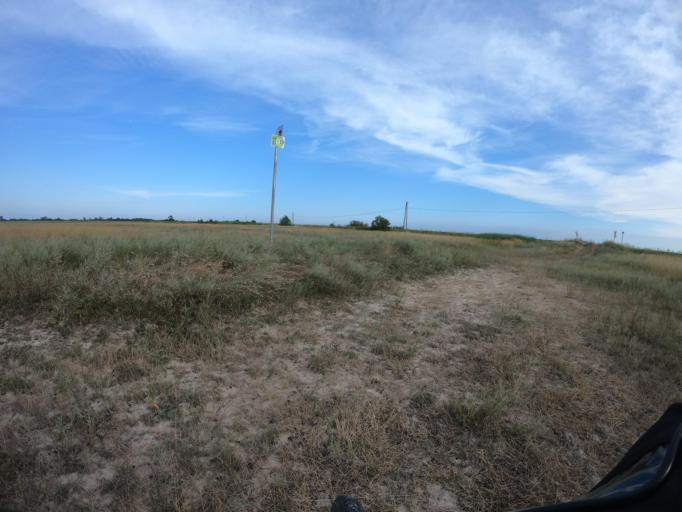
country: HU
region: Hajdu-Bihar
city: Tiszacsege
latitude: 47.6112
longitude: 21.0352
